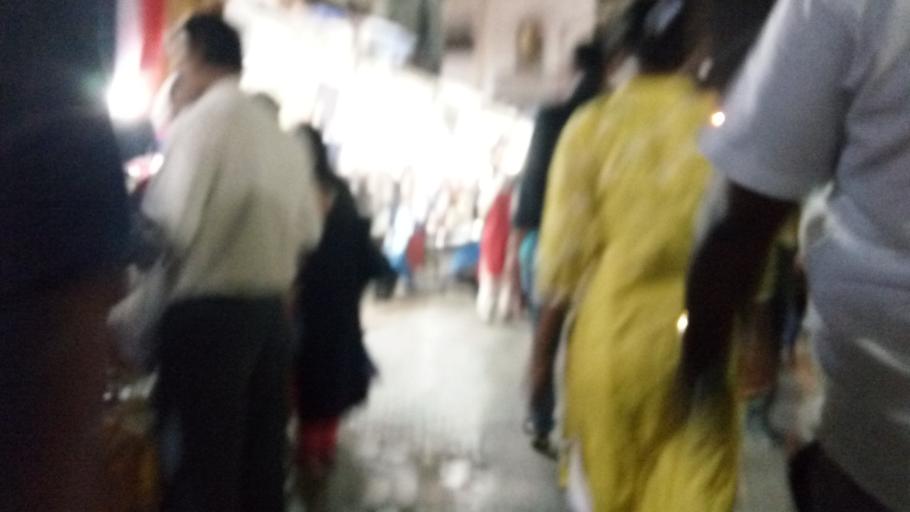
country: IN
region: Maharashtra
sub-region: Thane
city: Dombivli
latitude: 19.2176
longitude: 73.0880
